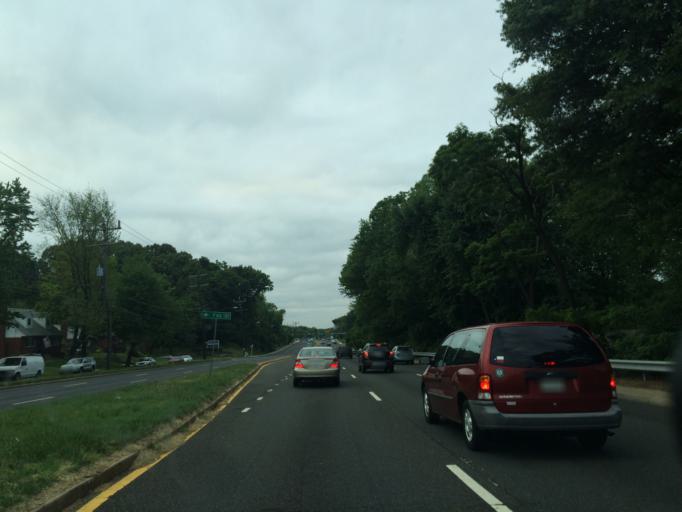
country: US
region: Maryland
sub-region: Prince George's County
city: Adelphi
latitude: 39.0095
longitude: -76.9796
